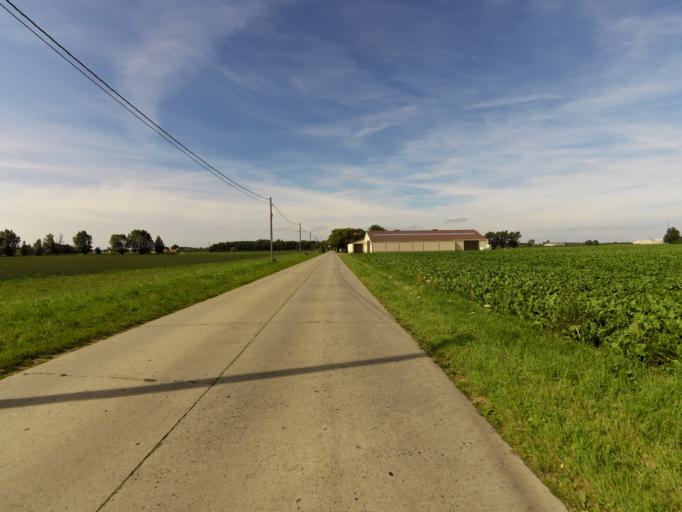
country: BE
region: Flanders
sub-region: Provincie West-Vlaanderen
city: Koekelare
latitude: 51.0418
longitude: 2.9746
